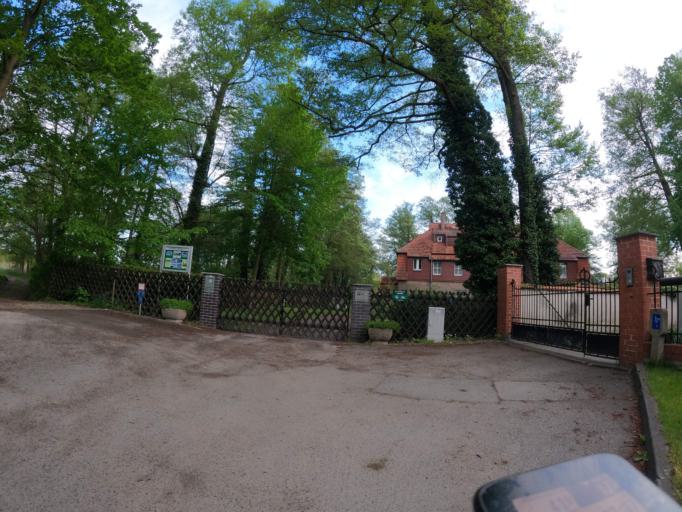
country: DE
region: Brandenburg
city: Konigs Wusterhausen
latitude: 52.3002
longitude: 13.6458
